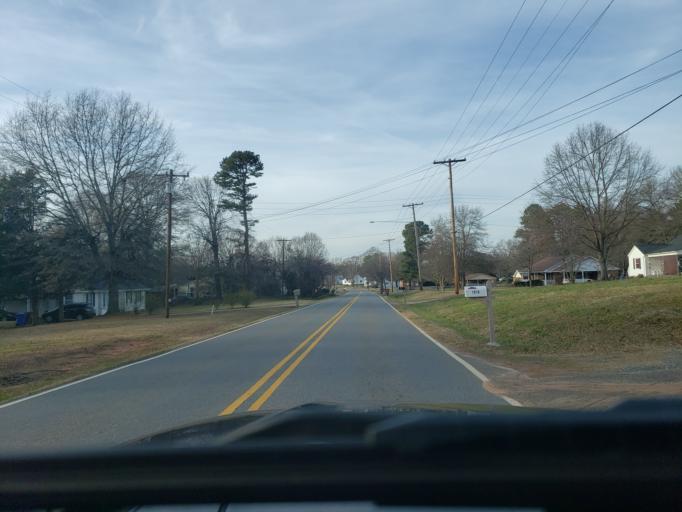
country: US
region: North Carolina
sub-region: Cleveland County
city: Shelby
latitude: 35.2768
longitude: -81.5068
